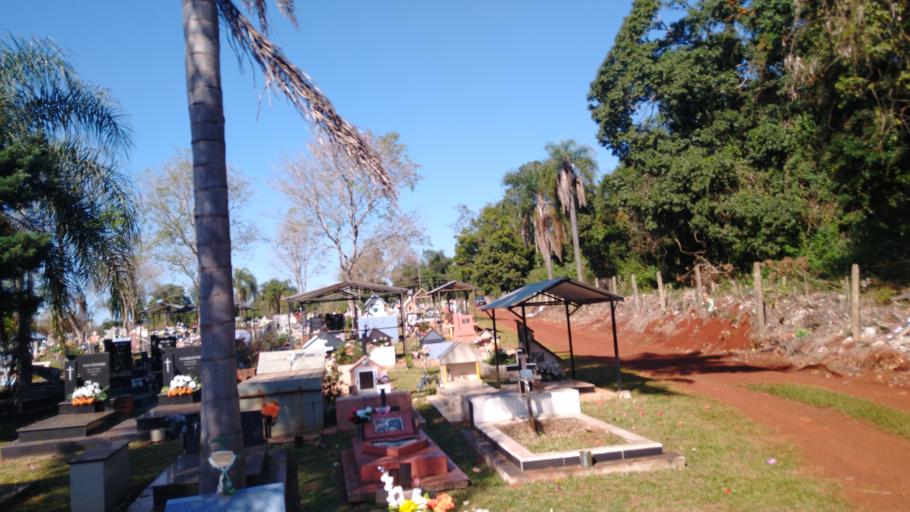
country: AR
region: Misiones
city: Puerto Libertad
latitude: -25.9698
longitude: -54.5416
